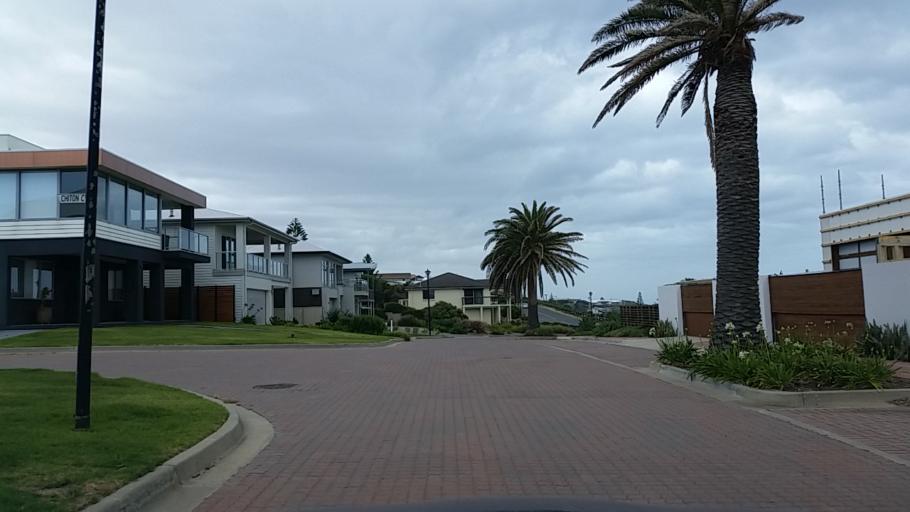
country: AU
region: South Australia
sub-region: Alexandrina
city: Port Elliot
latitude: -35.5351
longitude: 138.6715
